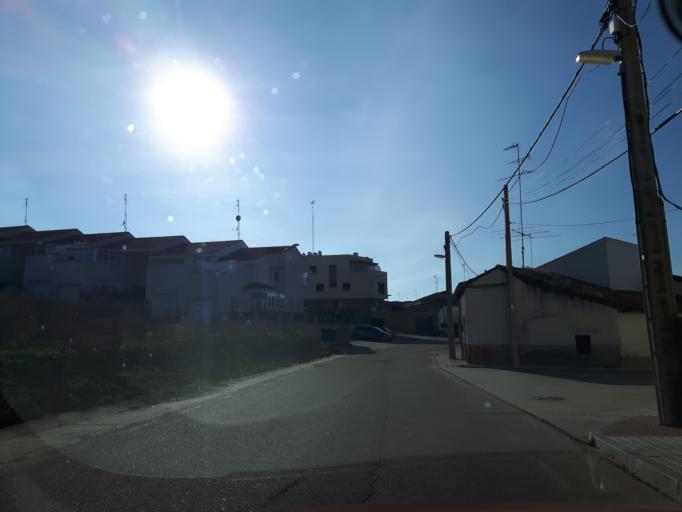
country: ES
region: Castille and Leon
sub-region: Provincia de Salamanca
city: San Cristobal de la Cuesta
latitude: 41.0294
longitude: -5.6161
